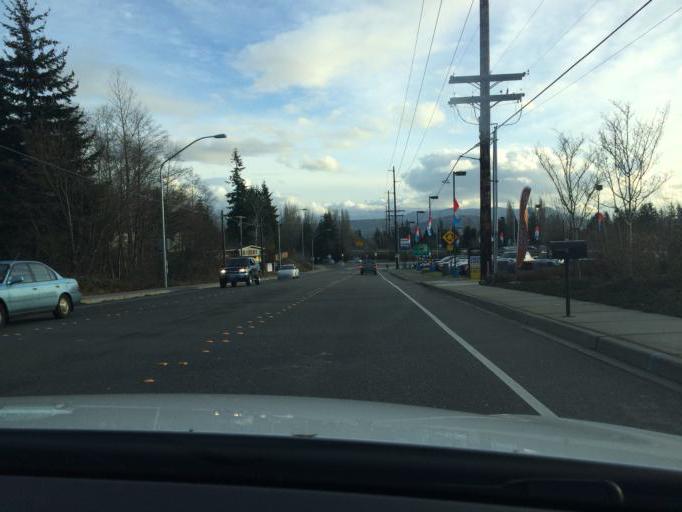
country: US
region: Washington
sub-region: Whatcom County
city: Bellingham
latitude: 48.7864
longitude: -122.5053
